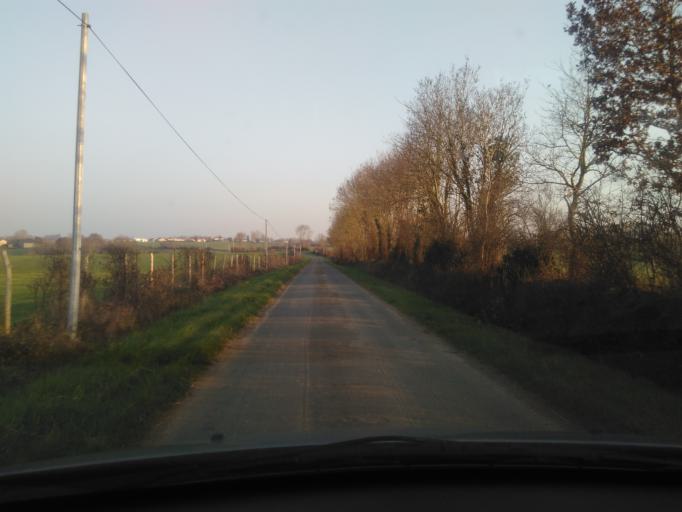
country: FR
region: Pays de la Loire
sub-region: Departement de la Vendee
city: Chantonnay
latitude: 46.6590
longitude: -1.0056
